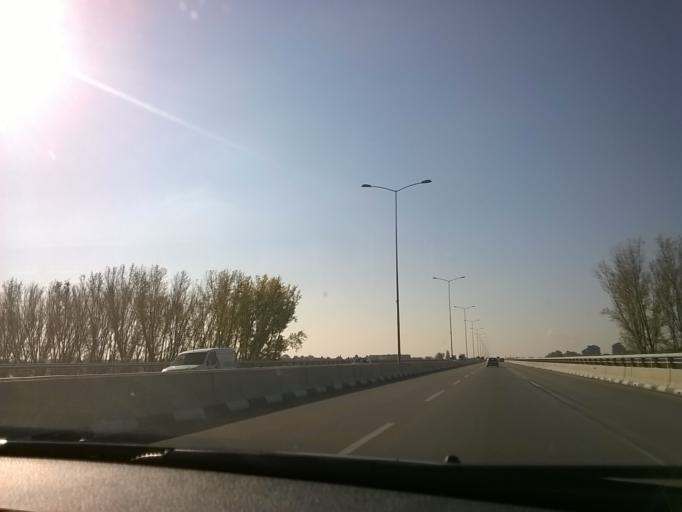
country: RS
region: Central Serbia
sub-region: Belgrade
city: Zemun
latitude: 44.8686
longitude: 20.3845
